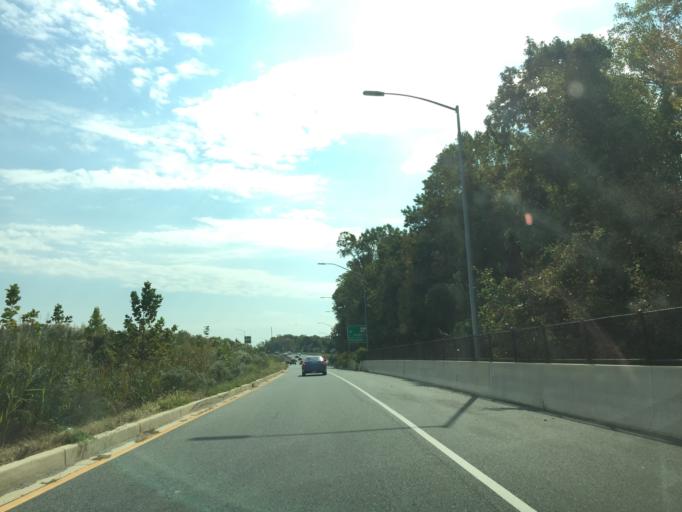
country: US
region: Maryland
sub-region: Harford County
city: Bel Air South
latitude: 39.4669
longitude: -76.3150
